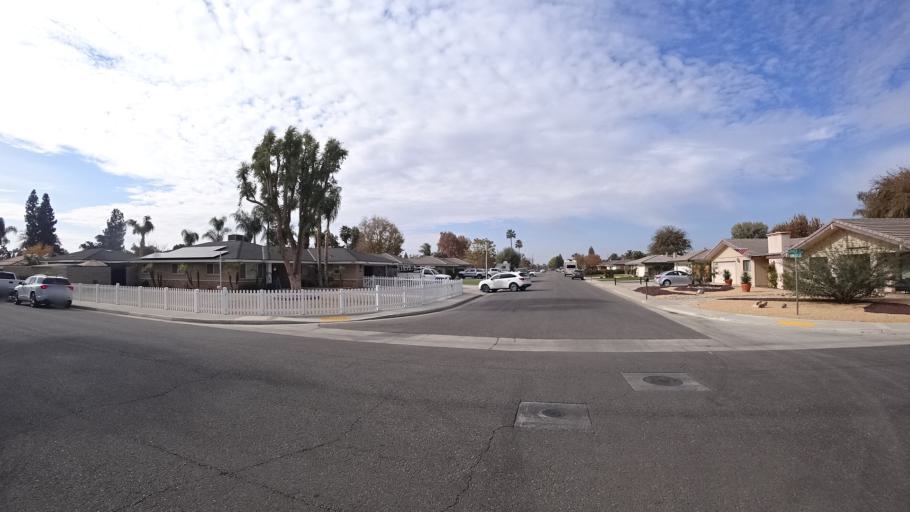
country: US
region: California
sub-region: Kern County
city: Greenacres
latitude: 35.4105
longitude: -119.0868
